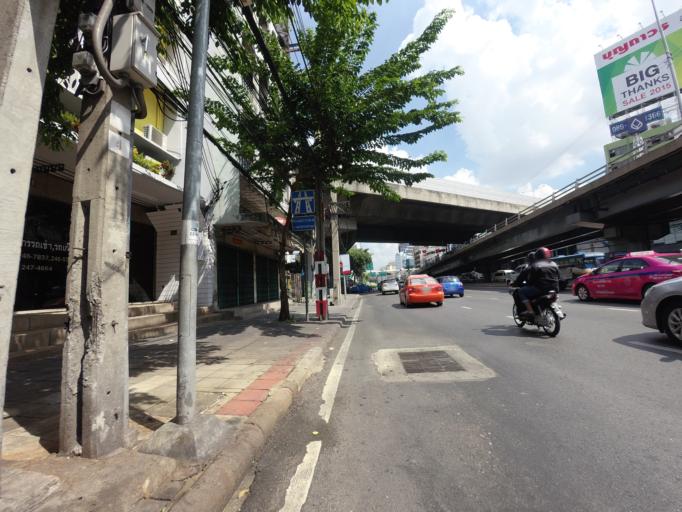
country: TH
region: Bangkok
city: Ratchathewi
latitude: 13.7629
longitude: 100.5435
